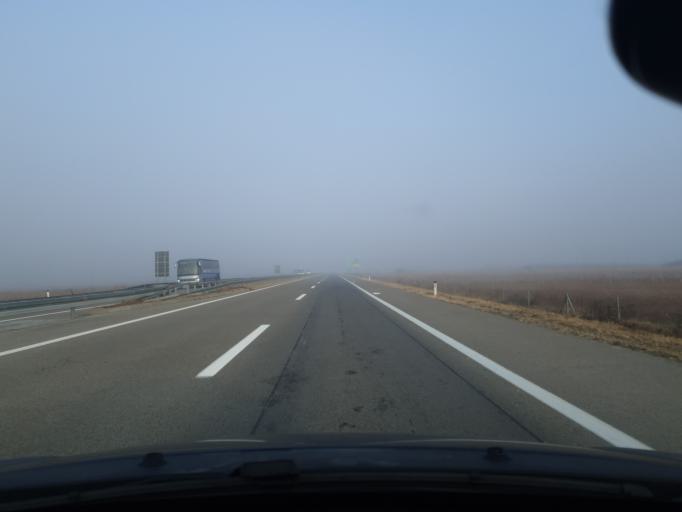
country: RS
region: Central Serbia
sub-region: Jablanicki Okrug
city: Leskovac
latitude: 43.0840
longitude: 21.9475
